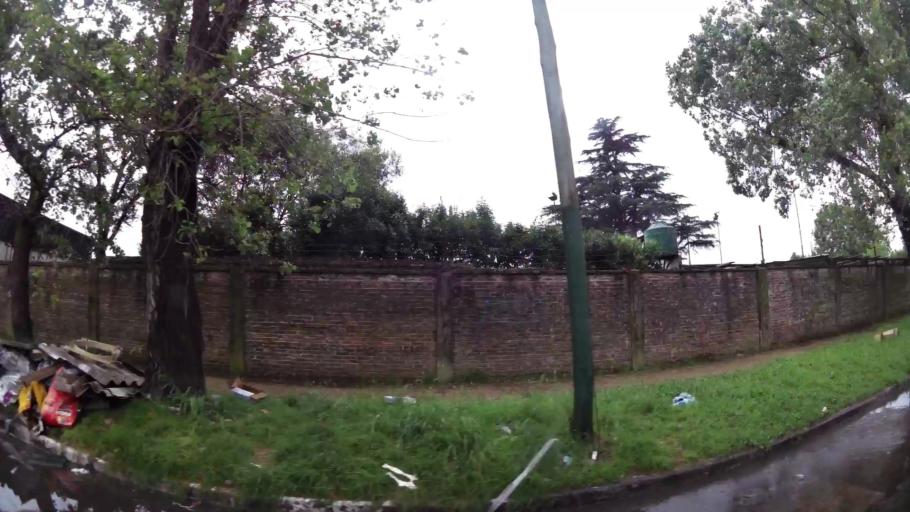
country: AR
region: Buenos Aires
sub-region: Partido de Lomas de Zamora
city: Lomas de Zamora
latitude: -34.7551
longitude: -58.3876
